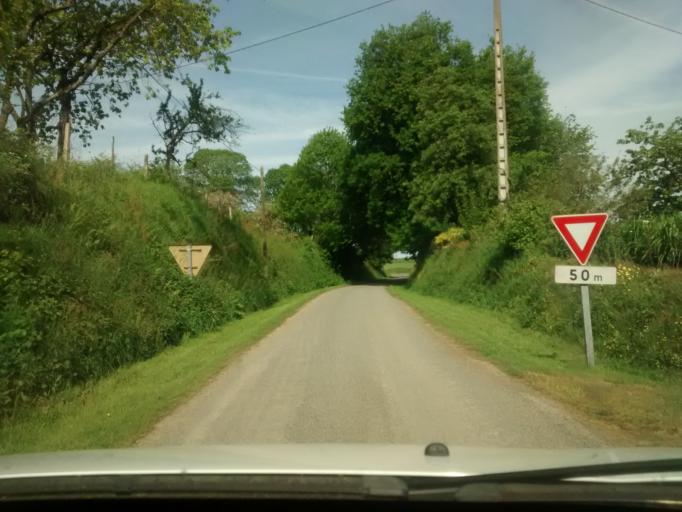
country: FR
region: Brittany
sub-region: Departement d'Ille-et-Vilaine
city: Romagne
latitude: 48.3353
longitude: -1.2476
